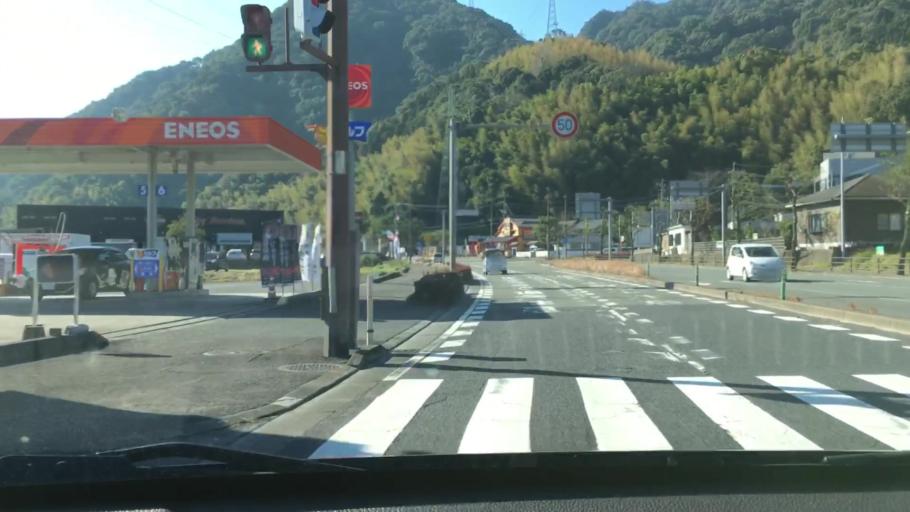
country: JP
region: Kagoshima
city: Kajiki
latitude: 31.7043
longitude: 130.6122
